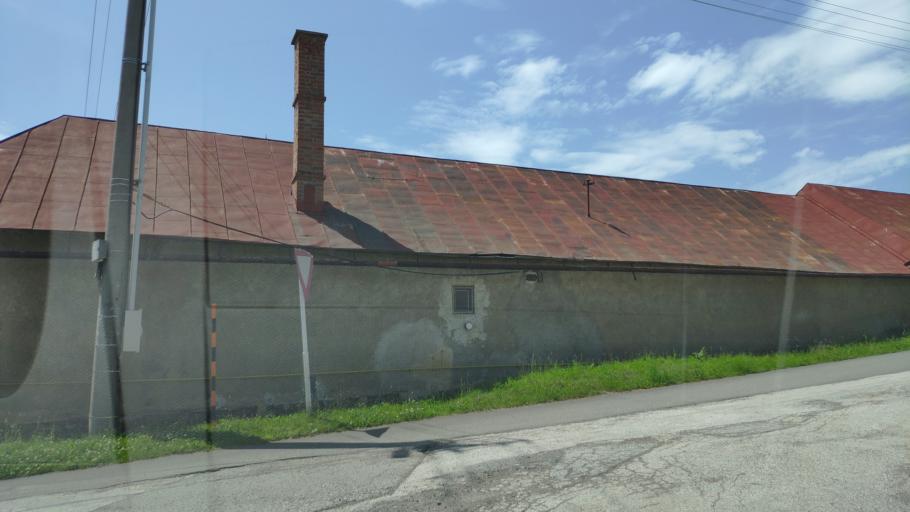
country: SK
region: Kosicky
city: Medzev
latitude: 48.7141
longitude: 20.9754
